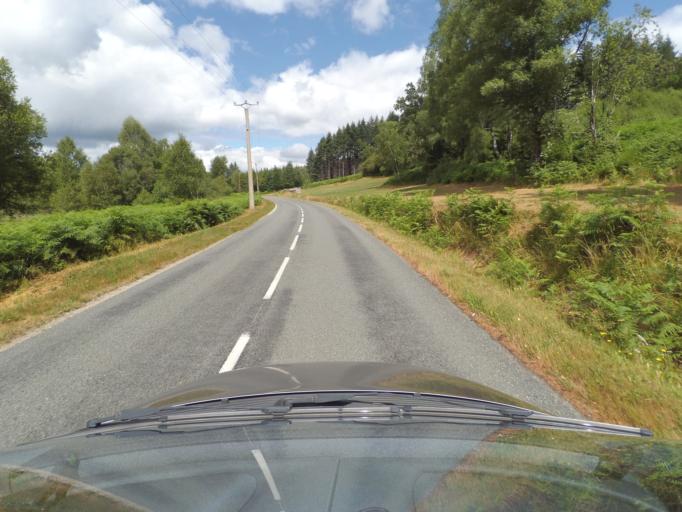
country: FR
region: Limousin
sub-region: Departement de la Haute-Vienne
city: Peyrat-le-Chateau
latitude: 45.8709
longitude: 1.8996
